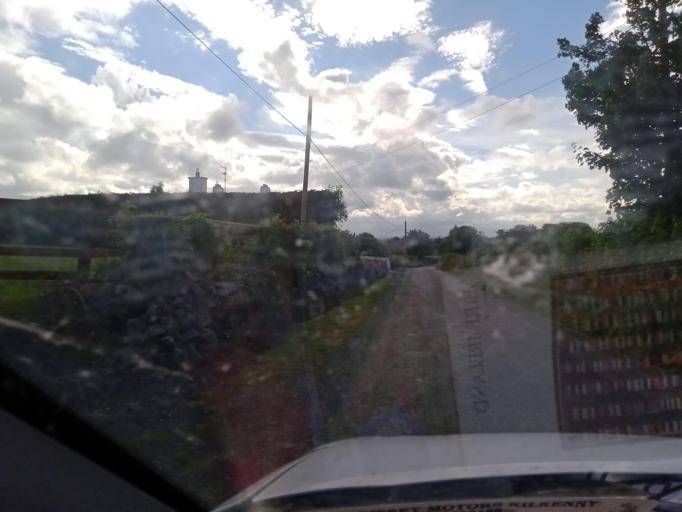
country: IE
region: Leinster
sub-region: Laois
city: Rathdowney
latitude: 52.7764
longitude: -7.5327
